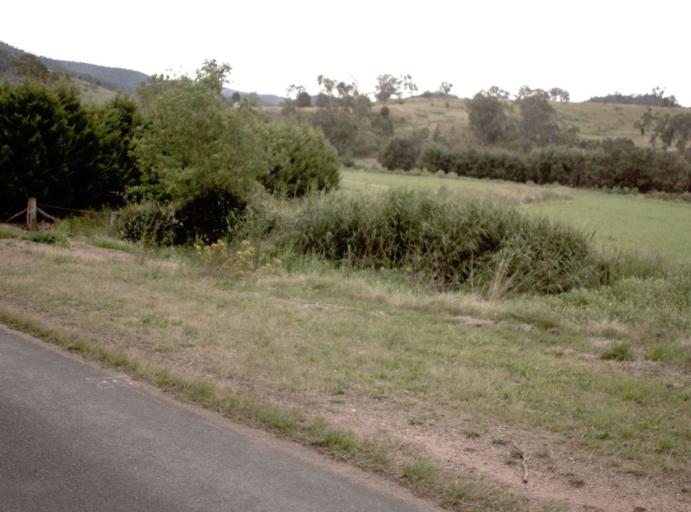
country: AU
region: Victoria
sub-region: East Gippsland
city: Bairnsdale
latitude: -37.4540
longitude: 147.2513
